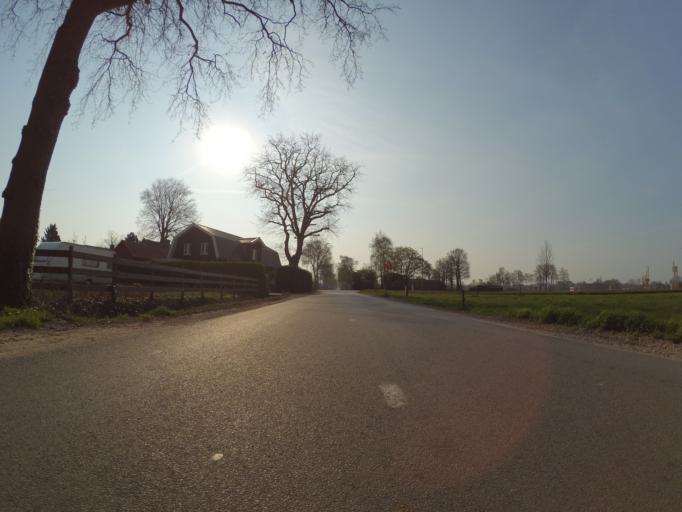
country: NL
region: Gelderland
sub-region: Gemeente Barneveld
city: Voorthuizen
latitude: 52.1807
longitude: 5.5873
